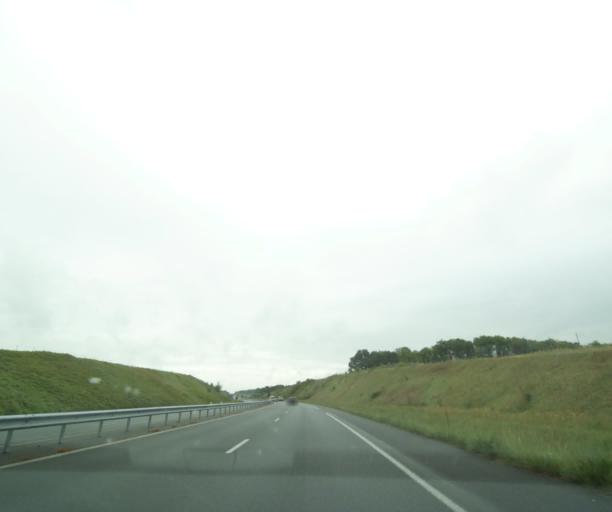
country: FR
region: Poitou-Charentes
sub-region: Departement de la Charente-Maritime
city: Nieul-les-Saintes
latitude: 45.6979
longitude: -0.7354
